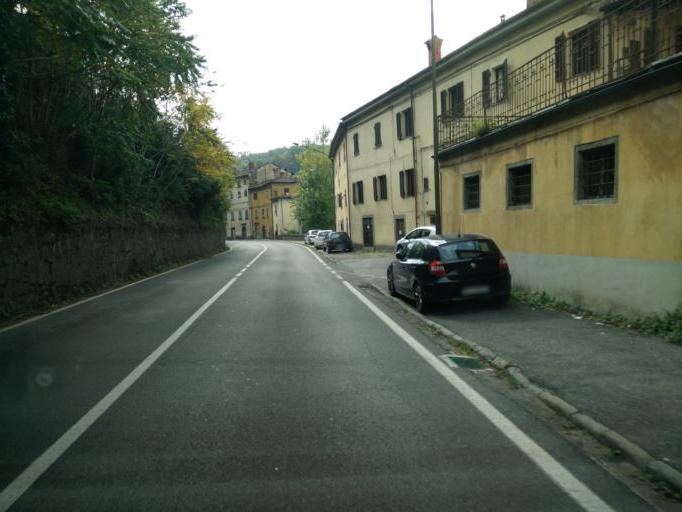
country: IT
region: Tuscany
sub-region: Provincia di Massa-Carrara
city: Pontremoli
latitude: 44.3659
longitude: 9.8851
